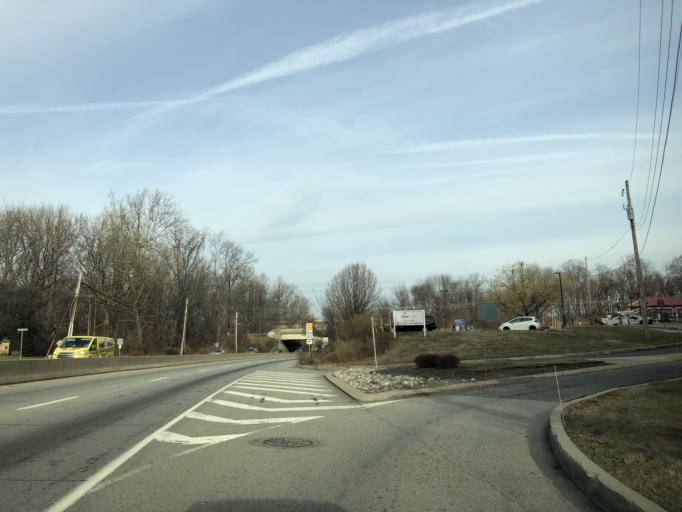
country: US
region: Pennsylvania
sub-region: Chester County
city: Exton
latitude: 40.0177
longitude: -75.6220
